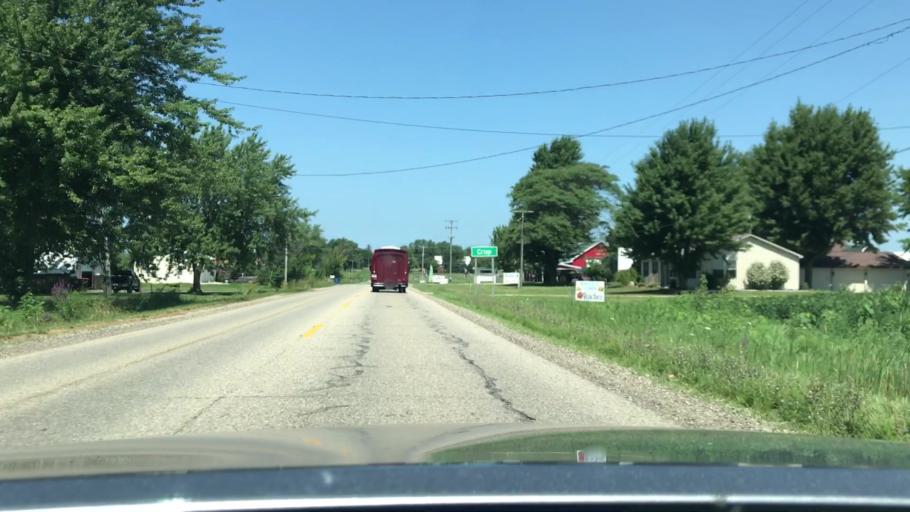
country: US
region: Michigan
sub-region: Ottawa County
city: Zeeland
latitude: 42.8750
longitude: -86.0799
